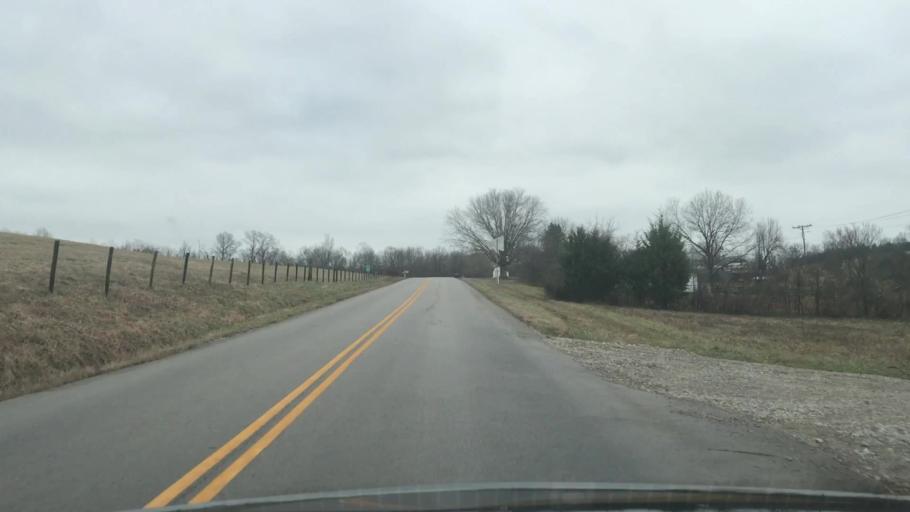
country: US
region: Kentucky
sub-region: Barren County
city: Glasgow
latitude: 36.9124
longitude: -85.8009
